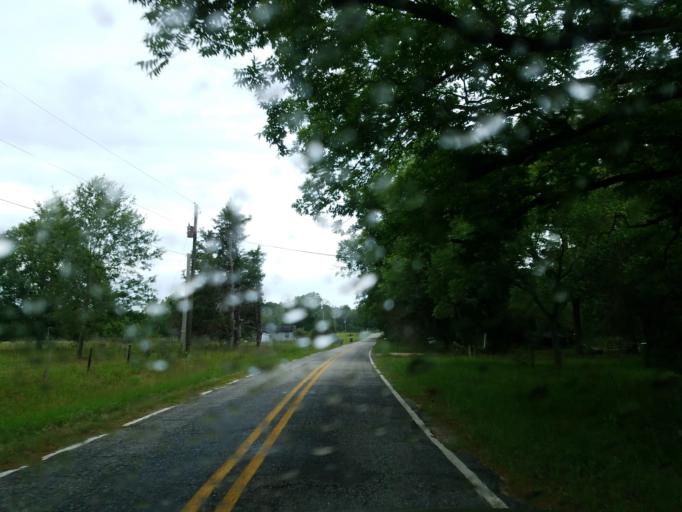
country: US
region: Georgia
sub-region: Crisp County
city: Cordele
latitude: 31.9318
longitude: -83.7032
